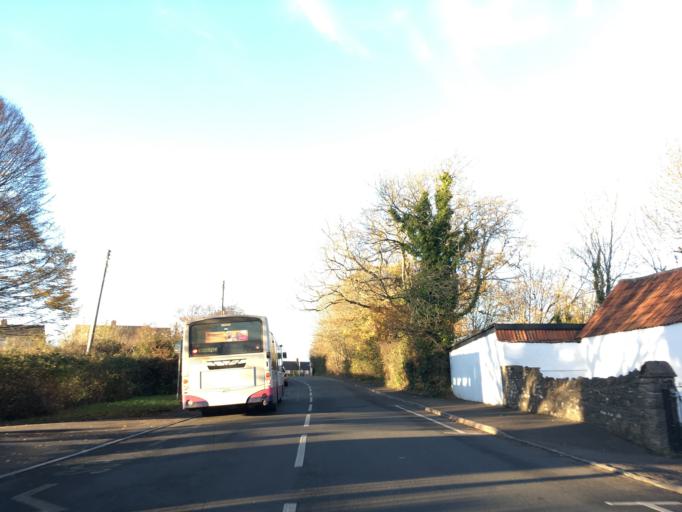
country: GB
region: England
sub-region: South Gloucestershire
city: Thornbury
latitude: 51.6120
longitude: -2.5128
